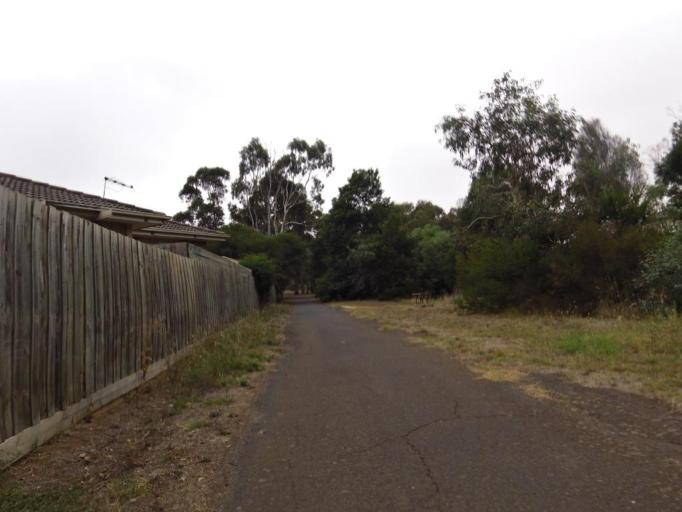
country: AU
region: Victoria
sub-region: Melton
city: Kurunjang
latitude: -37.6771
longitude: 144.5895
